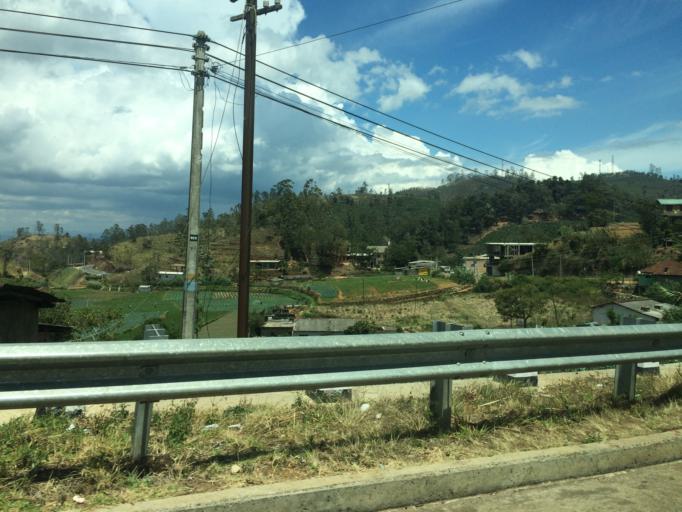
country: LK
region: Central
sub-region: Nuwara Eliya District
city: Nuwara Eliya
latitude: 6.9057
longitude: 80.8448
